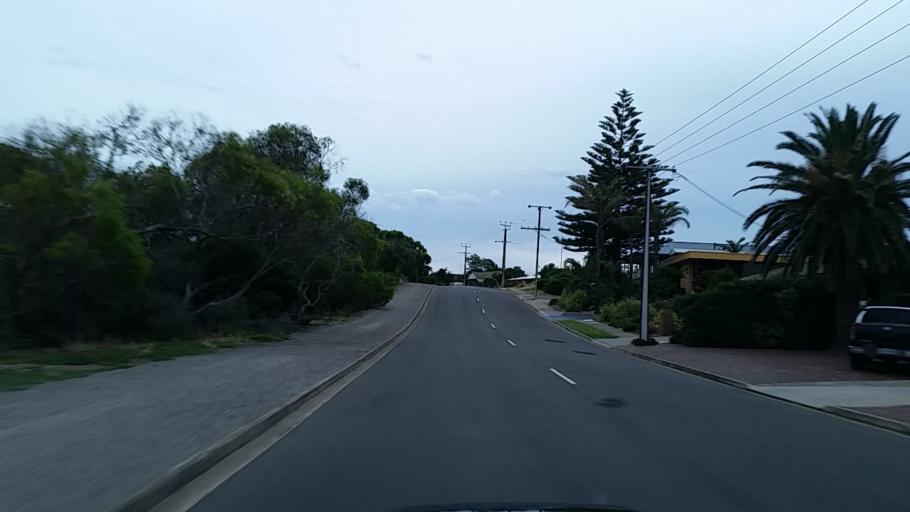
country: AU
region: South Australia
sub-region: Adelaide
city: Port Noarlunga
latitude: -35.1284
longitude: 138.4728
